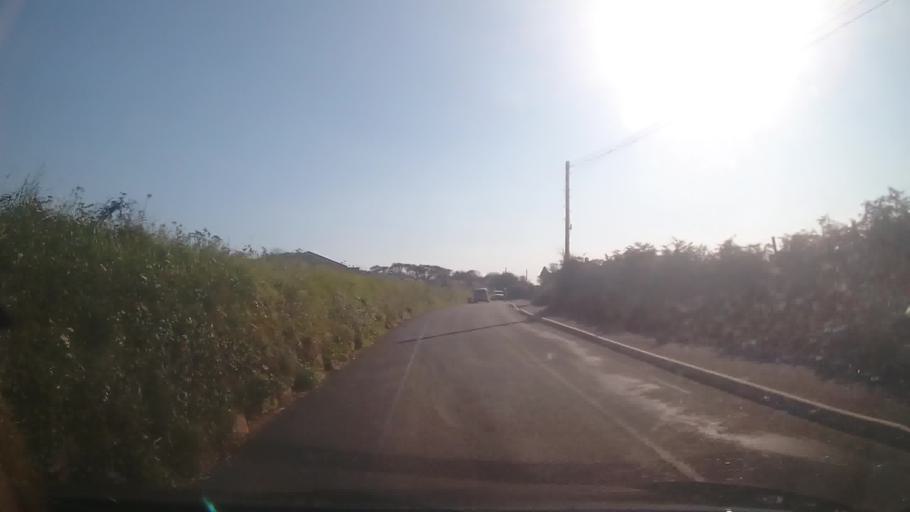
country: GB
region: Wales
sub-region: Pembrokeshire
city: Saint David's
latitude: 51.8871
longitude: -5.2593
